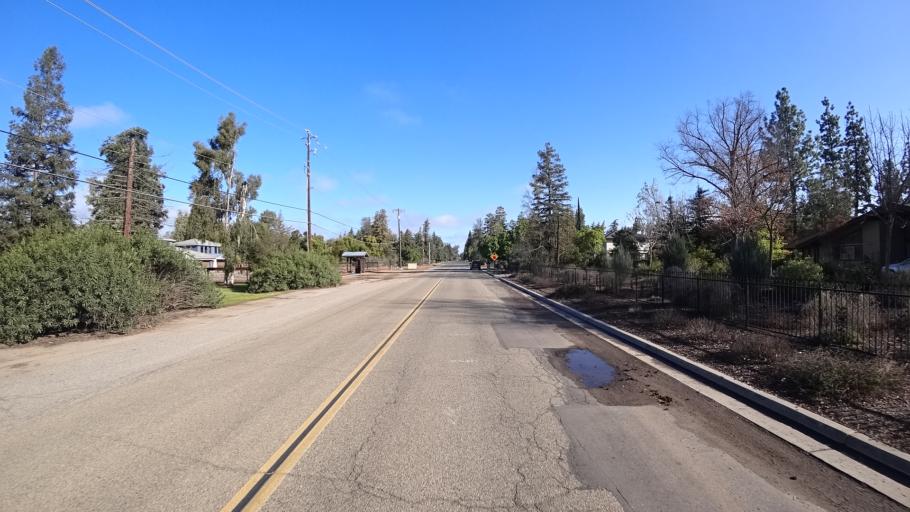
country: US
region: California
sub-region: Fresno County
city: Fresno
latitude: 36.8283
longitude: -119.8309
